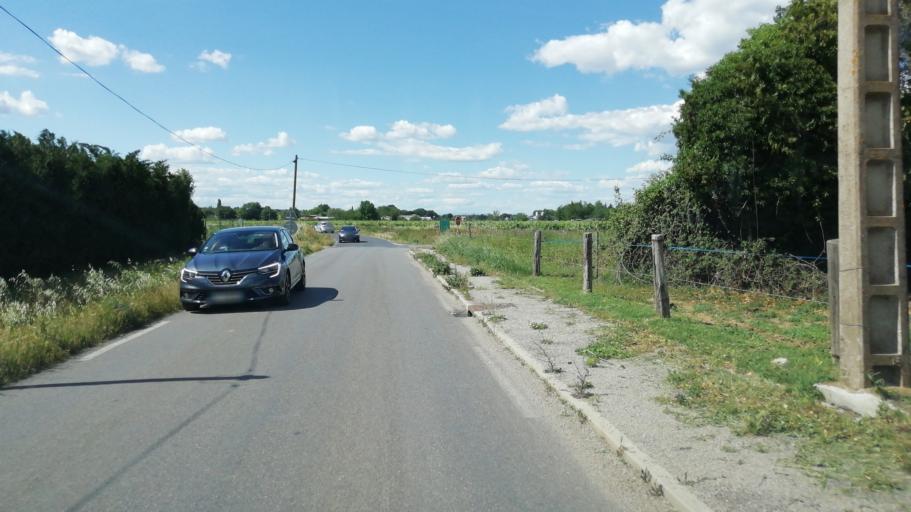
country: FR
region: Languedoc-Roussillon
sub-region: Departement de l'Herault
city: Lunel-Viel
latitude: 43.6696
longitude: 4.1032
